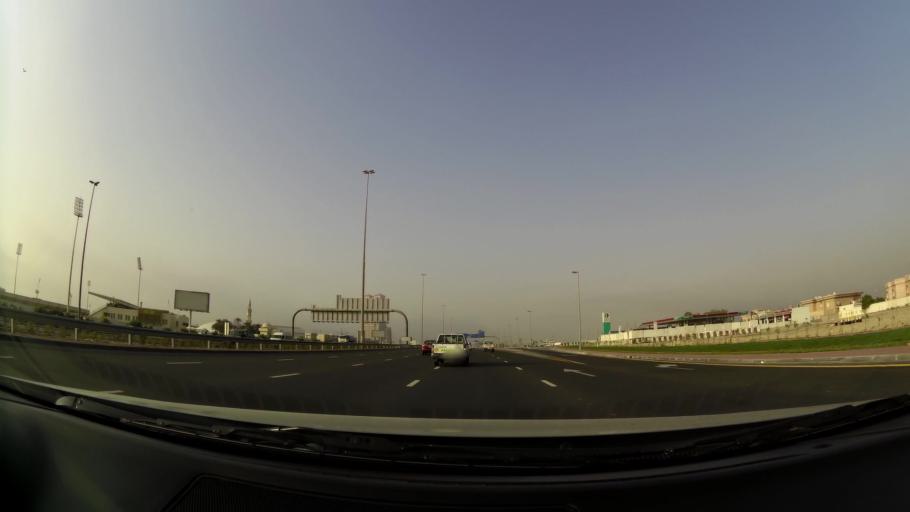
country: AE
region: Ash Shariqah
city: Sharjah
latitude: 25.2207
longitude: 55.3149
